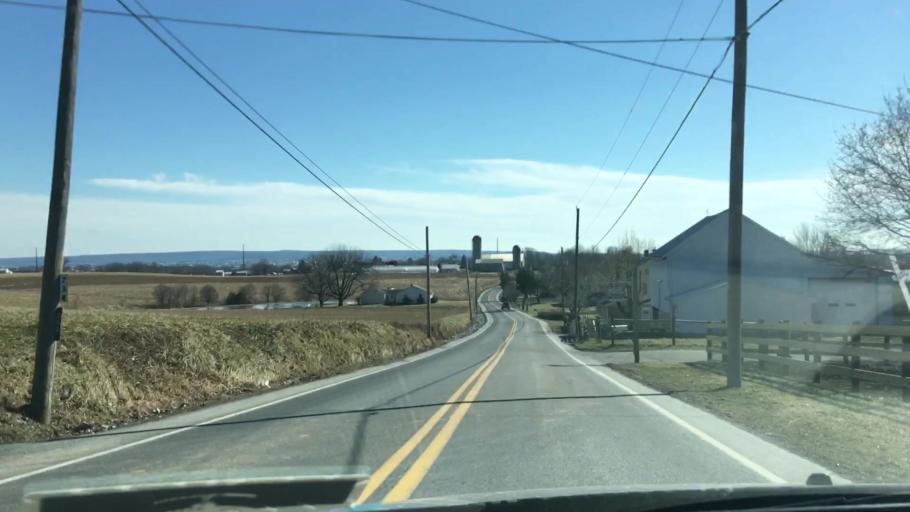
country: US
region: Pennsylvania
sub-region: Lancaster County
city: Reamstown
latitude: 40.1802
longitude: -76.1300
